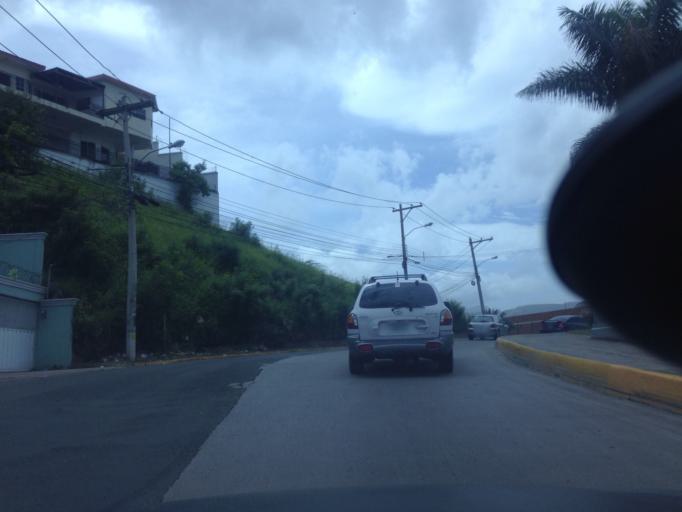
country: HN
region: Francisco Morazan
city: Tegucigalpa
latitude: 14.0777
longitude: -87.2011
